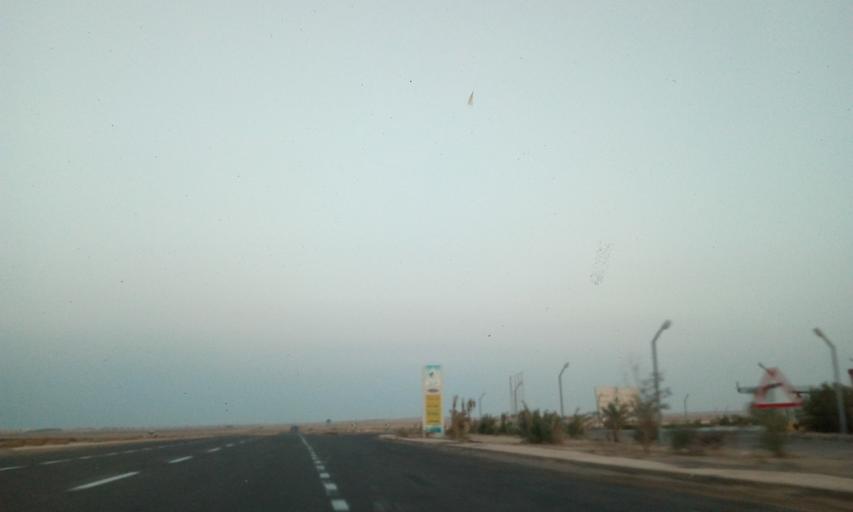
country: EG
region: Red Sea
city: El Gouna
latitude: 27.3301
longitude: 33.6648
